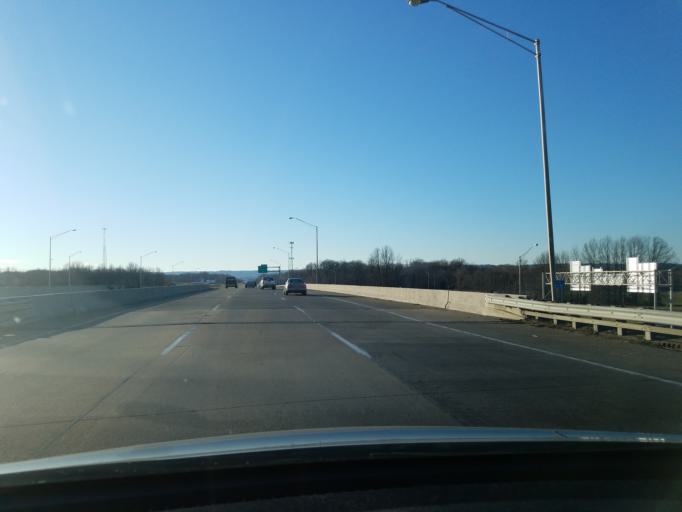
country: US
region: Indiana
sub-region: Clark County
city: Clarksville
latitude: 38.3459
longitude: -85.7535
